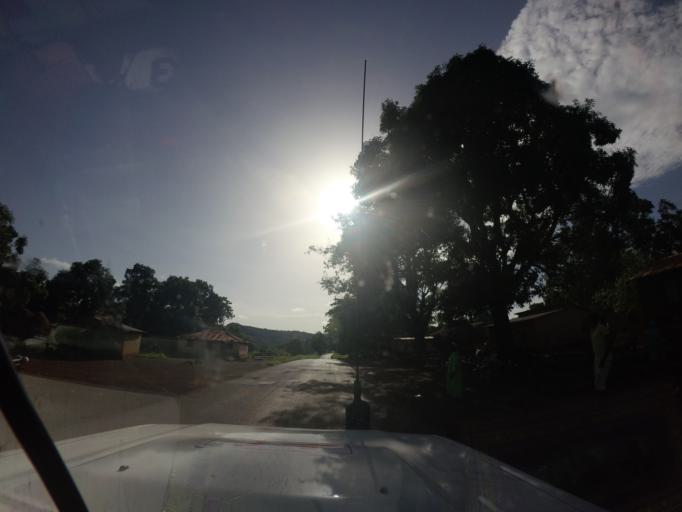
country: GN
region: Kindia
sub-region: Kindia
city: Kindia
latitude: 10.0707
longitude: -12.6020
